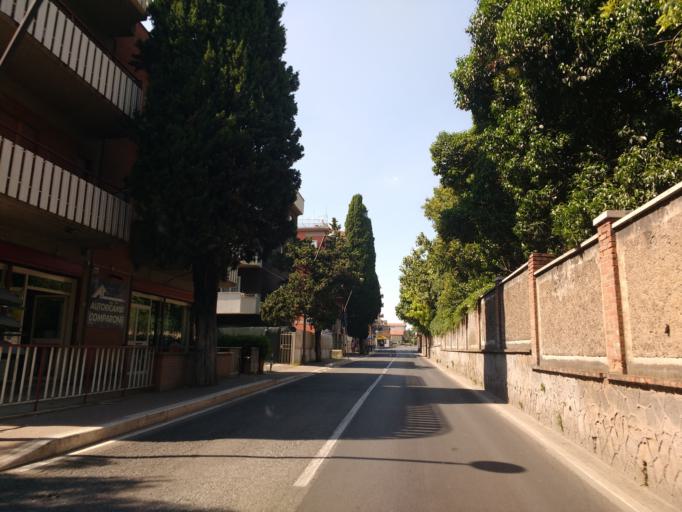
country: IT
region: Latium
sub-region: Citta metropolitana di Roma Capitale
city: Villa Adriana
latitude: 41.9558
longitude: 12.7757
